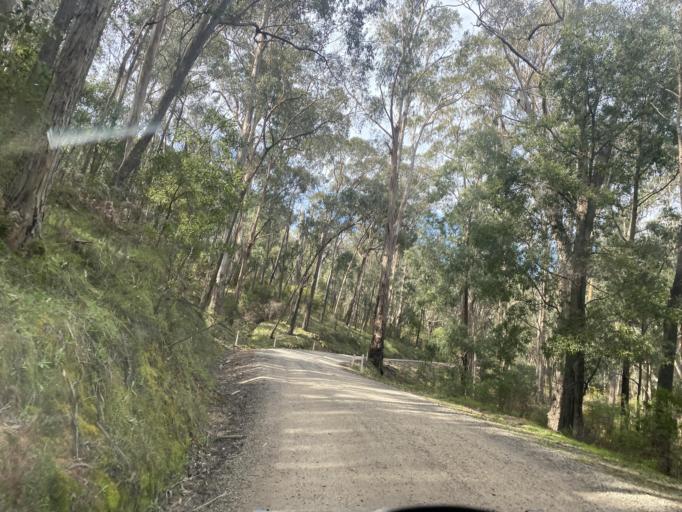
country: AU
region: Victoria
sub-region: Mansfield
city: Mansfield
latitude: -36.8244
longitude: 146.1473
